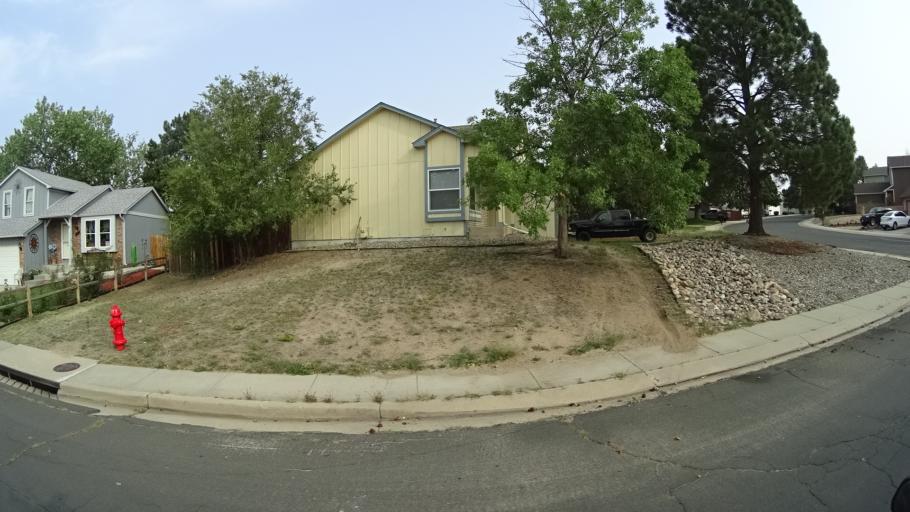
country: US
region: Colorado
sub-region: El Paso County
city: Stratmoor
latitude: 38.8076
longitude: -104.7491
